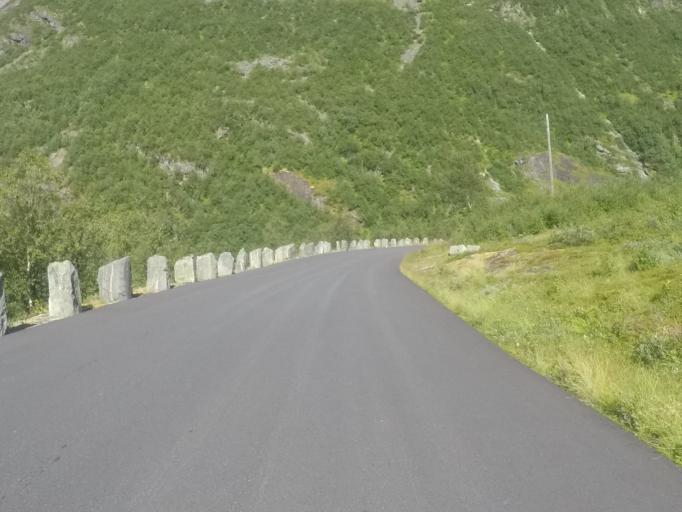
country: NO
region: More og Romsdal
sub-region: Norddal
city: Valldal
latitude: 61.9385
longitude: 7.2687
